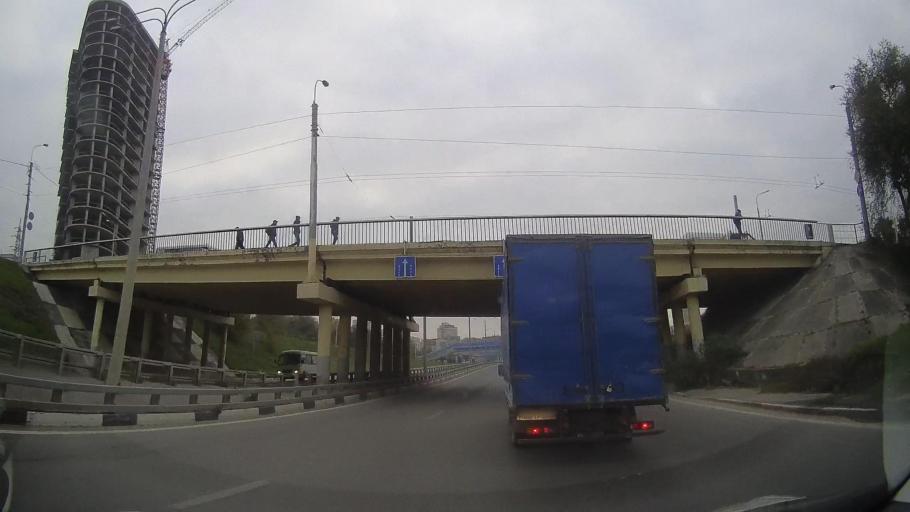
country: RU
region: Rostov
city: Rostov-na-Donu
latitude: 47.2220
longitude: 39.6917
